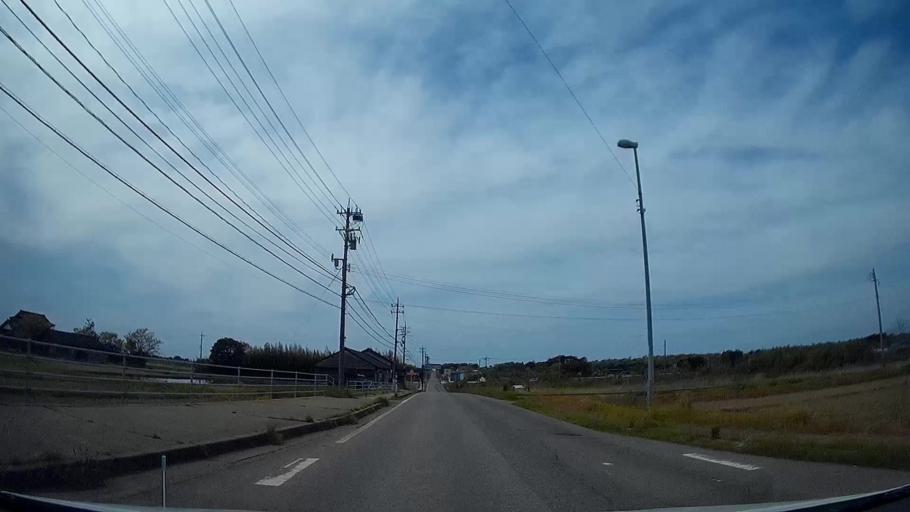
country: JP
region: Ishikawa
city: Hakui
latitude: 37.0118
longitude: 136.7601
